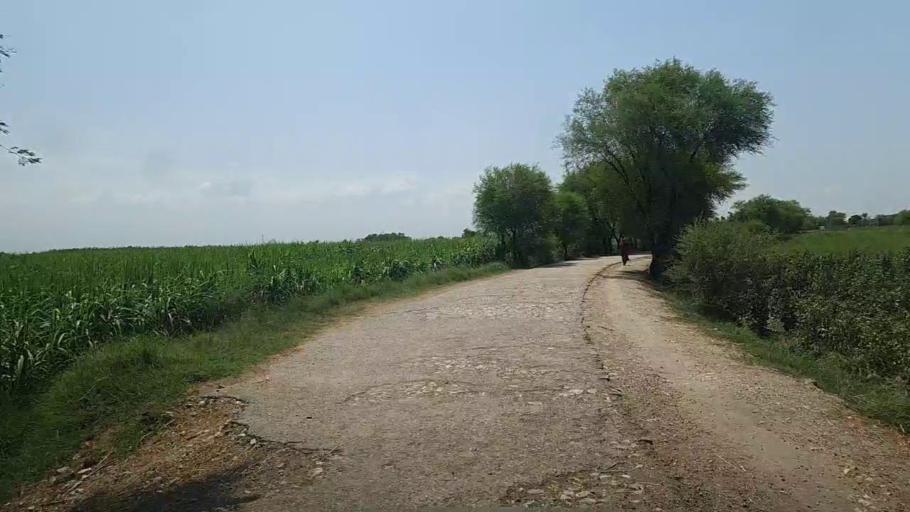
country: PK
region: Sindh
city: Ubauro
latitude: 28.2001
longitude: 69.8028
